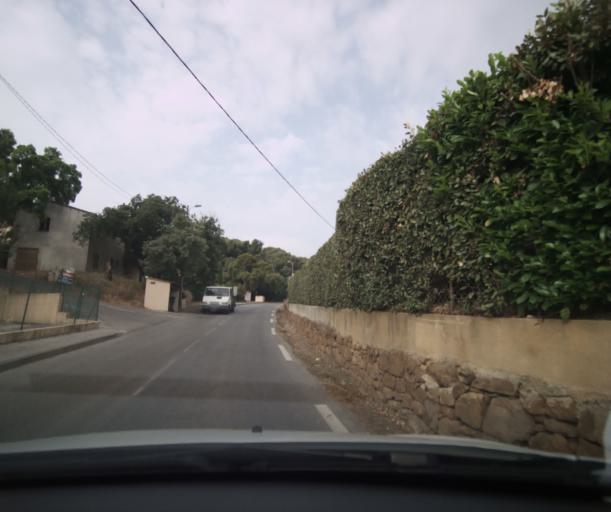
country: FR
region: Provence-Alpes-Cote d'Azur
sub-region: Departement du Var
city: Carqueiranne
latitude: 43.0947
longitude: 6.0676
